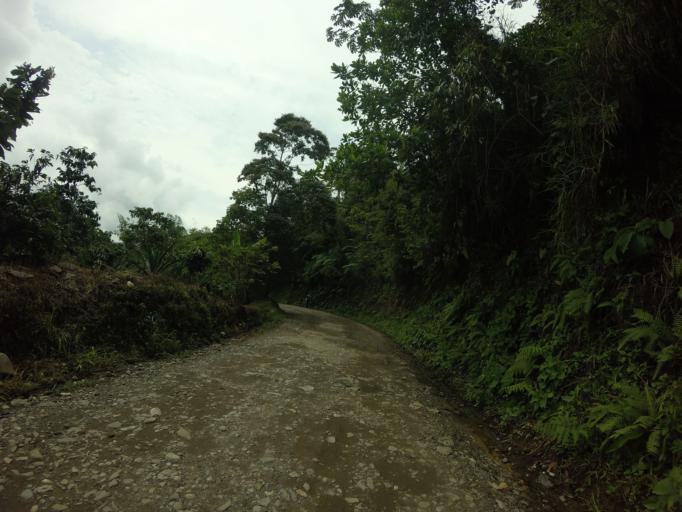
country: CO
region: Caldas
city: Victoria
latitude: 5.3105
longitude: -74.9659
